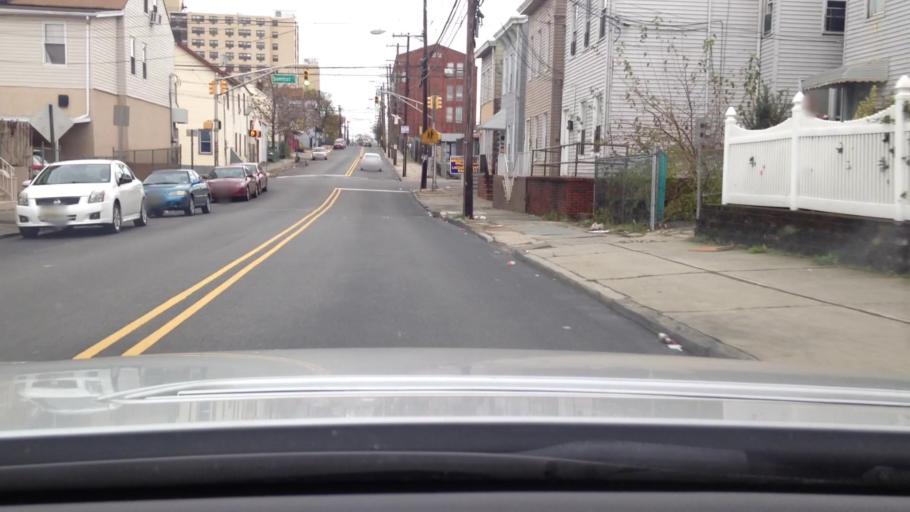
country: US
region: New Jersey
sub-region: Passaic County
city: Paterson
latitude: 40.9090
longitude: -74.1645
